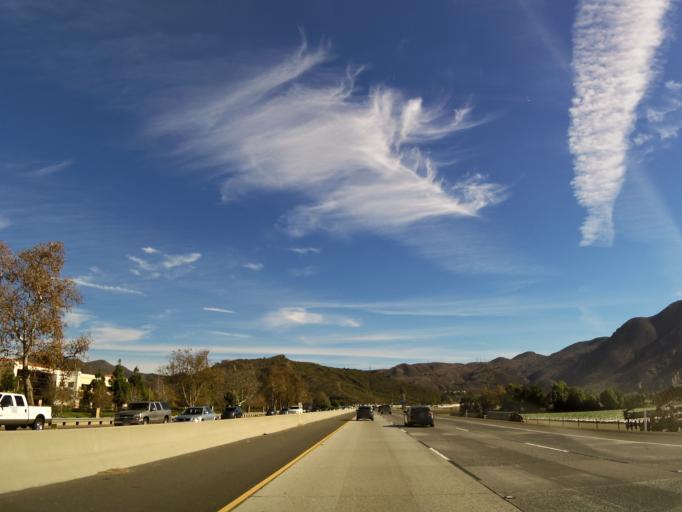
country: US
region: California
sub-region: Ventura County
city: Camarillo
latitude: 34.2109
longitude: -118.9994
